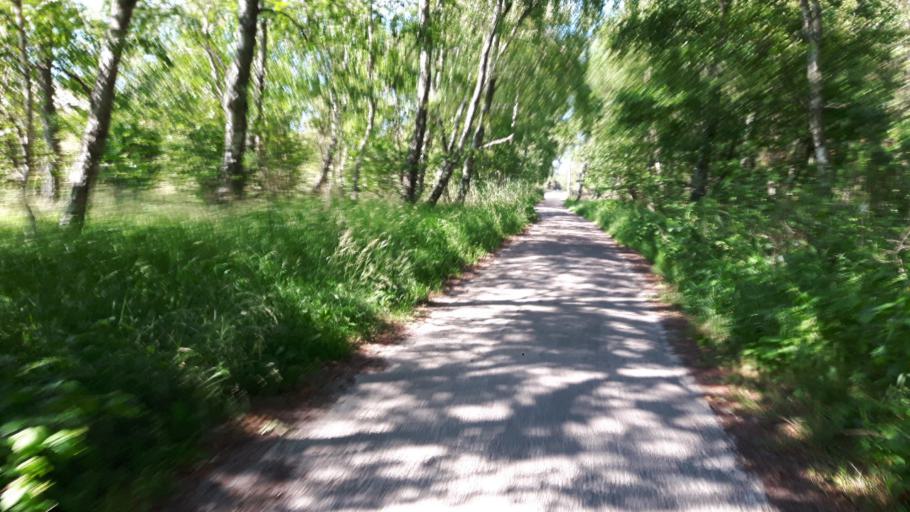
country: LT
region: Klaipedos apskritis
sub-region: Klaipeda
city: Klaipeda
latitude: 55.6885
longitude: 21.1035
